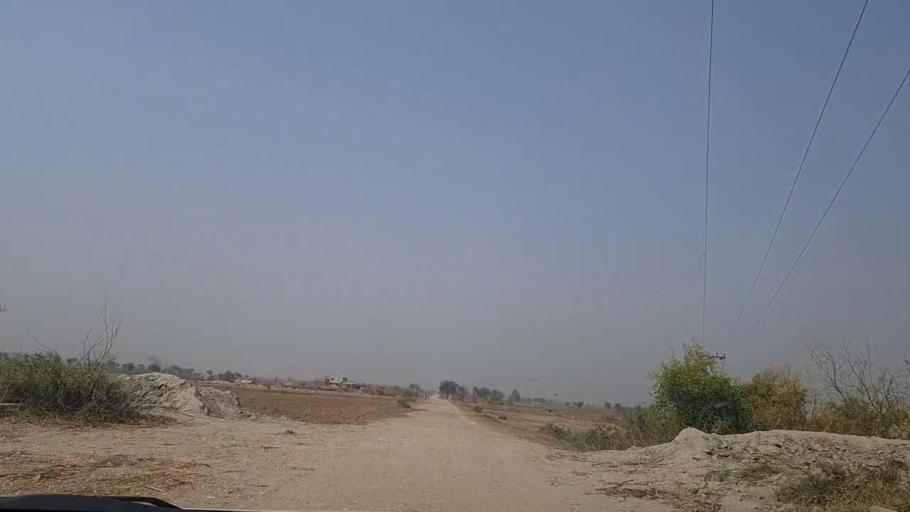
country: PK
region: Sindh
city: Pithoro
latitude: 25.5597
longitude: 69.2096
